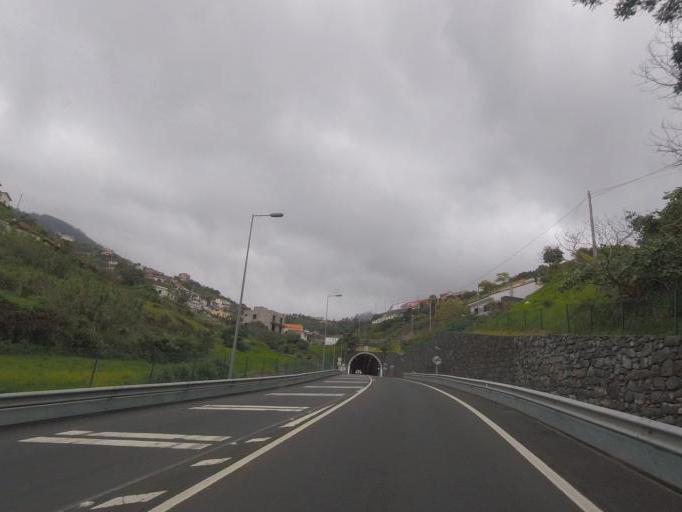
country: PT
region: Madeira
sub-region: Machico
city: Machico
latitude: 32.7320
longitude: -16.7848
